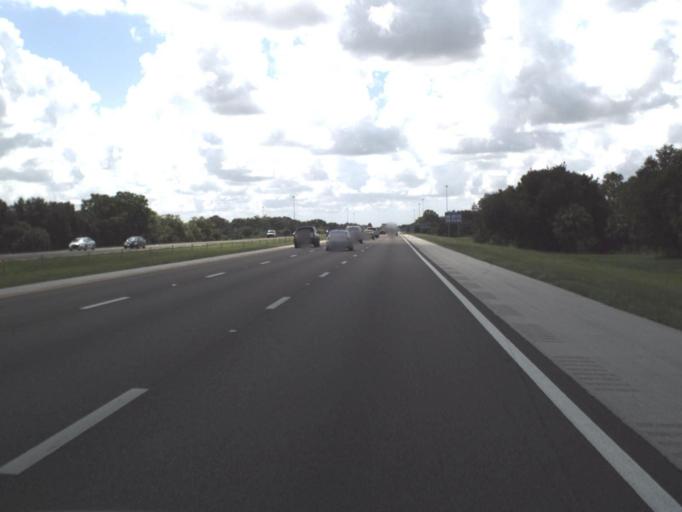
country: US
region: Florida
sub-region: Lee County
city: Bonita Springs
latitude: 26.3419
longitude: -81.7526
